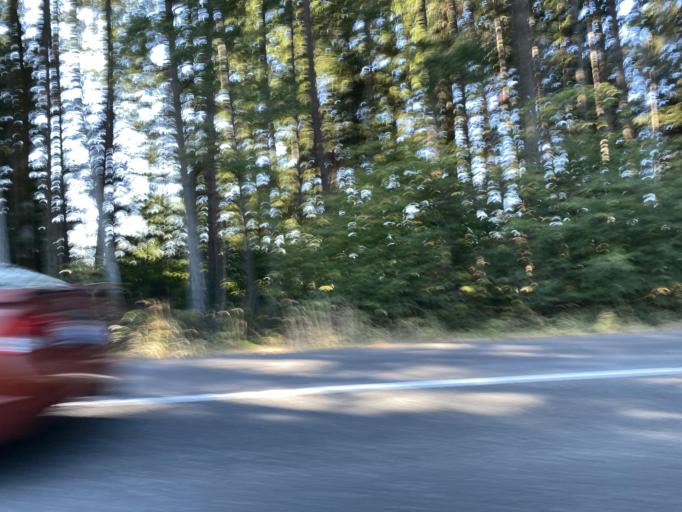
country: US
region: Washington
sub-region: Thurston County
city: Tanglewilde-Thompson Place
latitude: 46.9844
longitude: -122.7639
